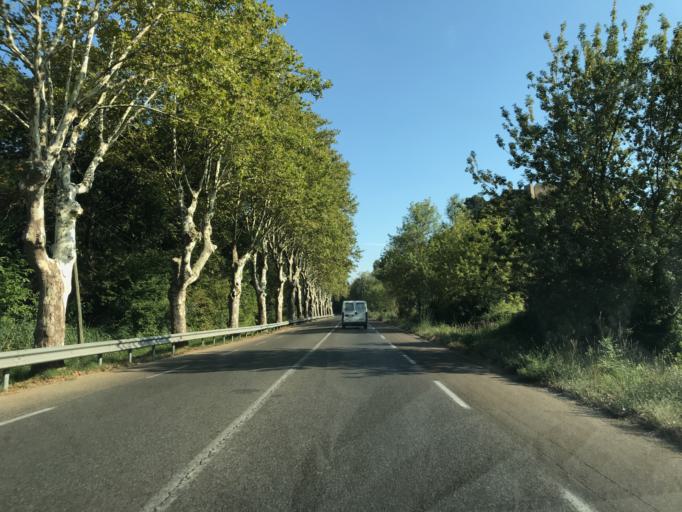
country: FR
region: Provence-Alpes-Cote d'Azur
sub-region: Departement des Bouches-du-Rhone
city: Saint-Chamas
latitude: 43.5674
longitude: 5.0243
